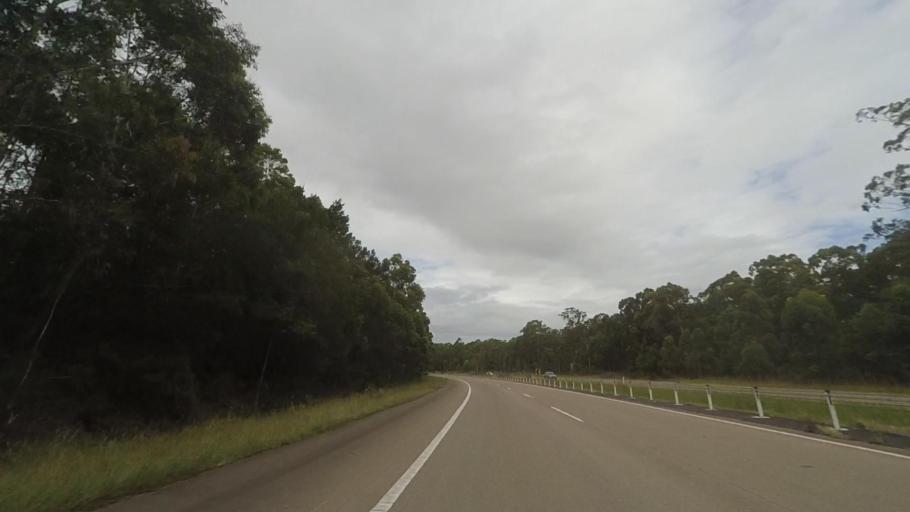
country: AU
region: New South Wales
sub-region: Port Stephens Shire
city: Medowie
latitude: -32.6508
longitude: 151.9054
